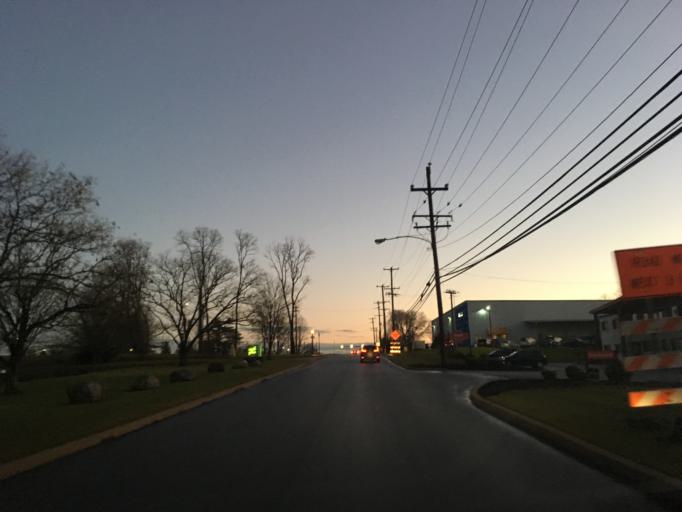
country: US
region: Pennsylvania
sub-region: Delaware County
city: Chester Heights
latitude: 39.8880
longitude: -75.5291
